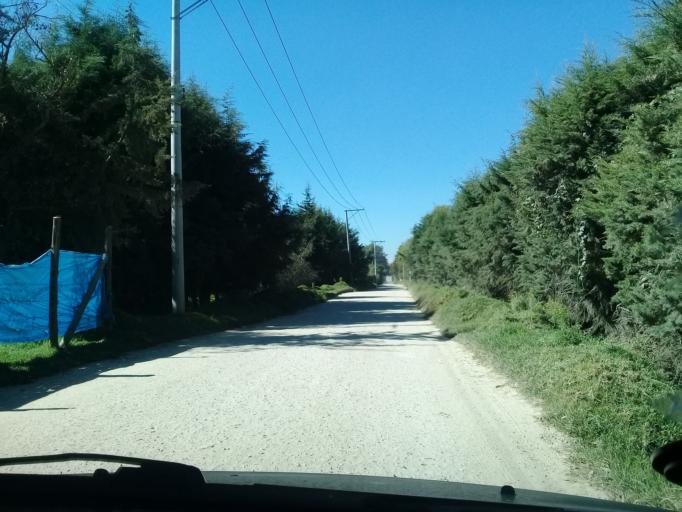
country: CO
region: Cundinamarca
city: Funza
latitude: 4.7384
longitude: -74.2311
